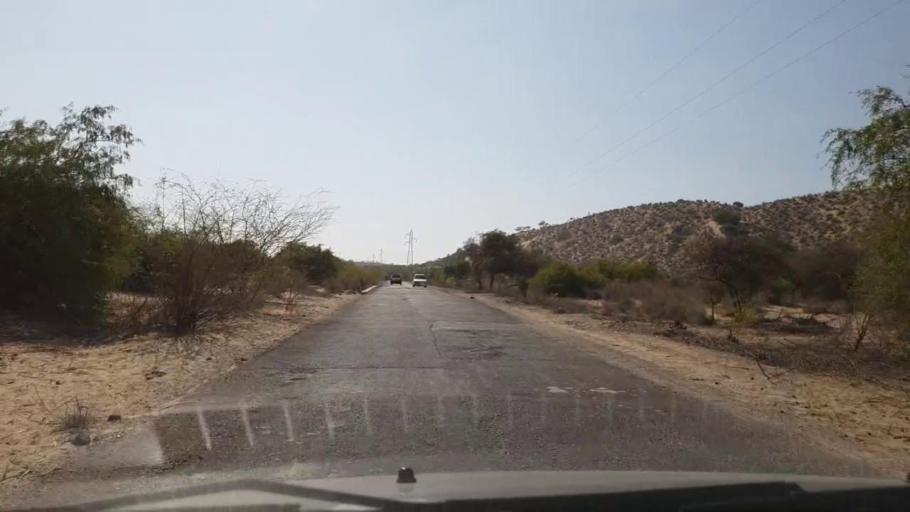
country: PK
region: Sindh
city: Mithi
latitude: 24.6423
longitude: 69.7454
